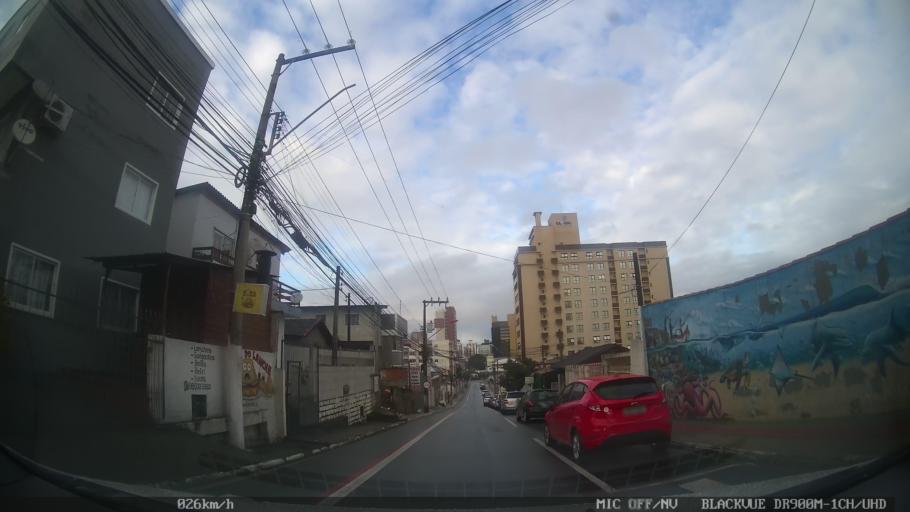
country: BR
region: Santa Catarina
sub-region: Sao Jose
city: Campinas
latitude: -27.5835
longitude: -48.6104
